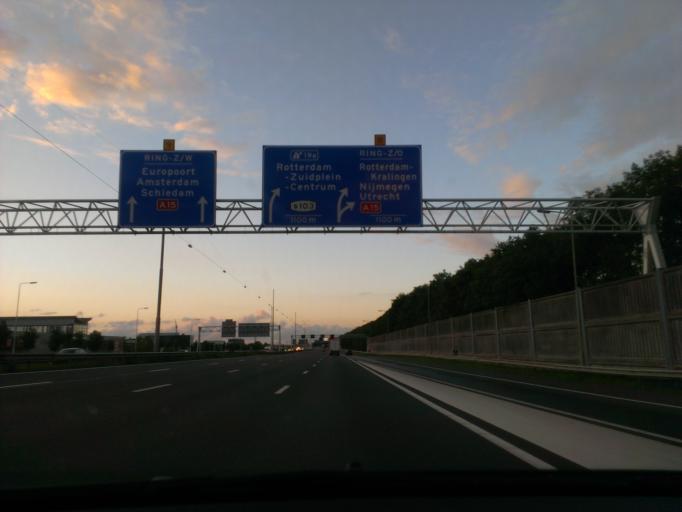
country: NL
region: South Holland
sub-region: Gemeente Barendrecht
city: Barendrecht
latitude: 51.8486
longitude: 4.5158
